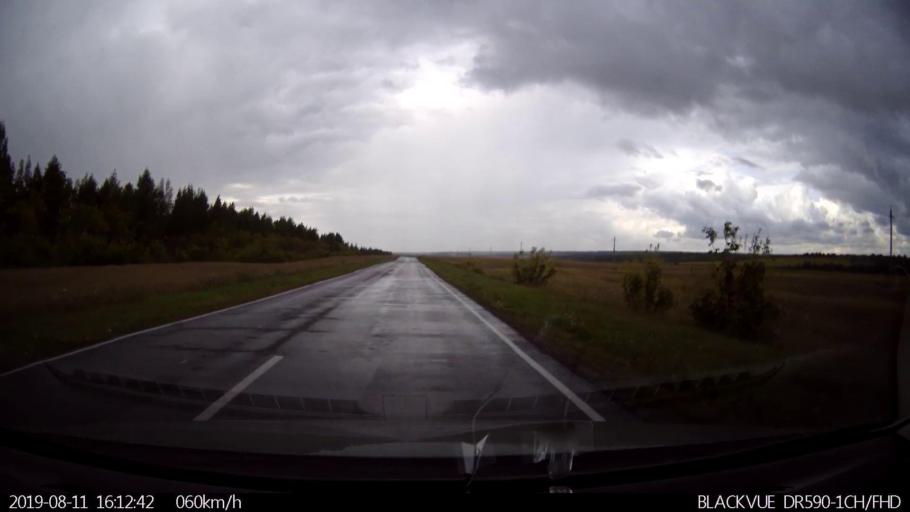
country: RU
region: Ulyanovsk
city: Ignatovka
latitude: 54.0137
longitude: 47.6396
